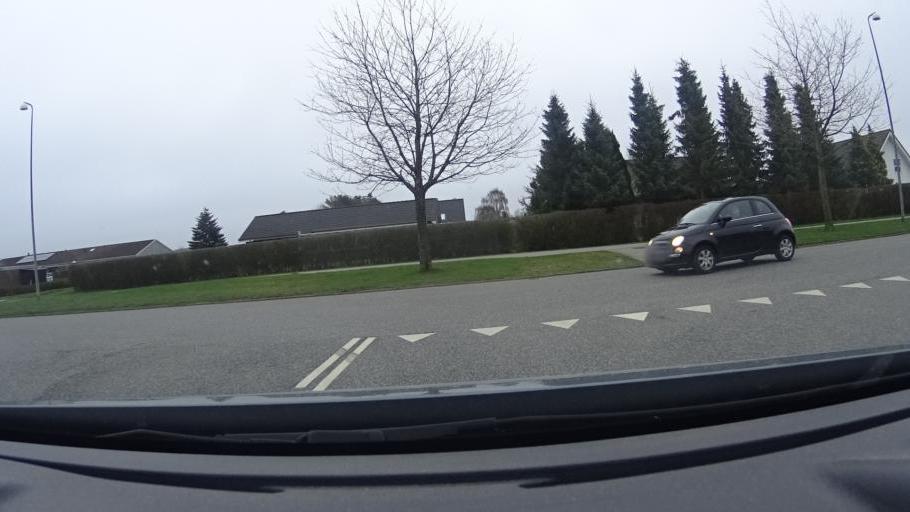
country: DK
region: South Denmark
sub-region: Vejle Kommune
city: Vejle
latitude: 55.7178
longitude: 9.6147
